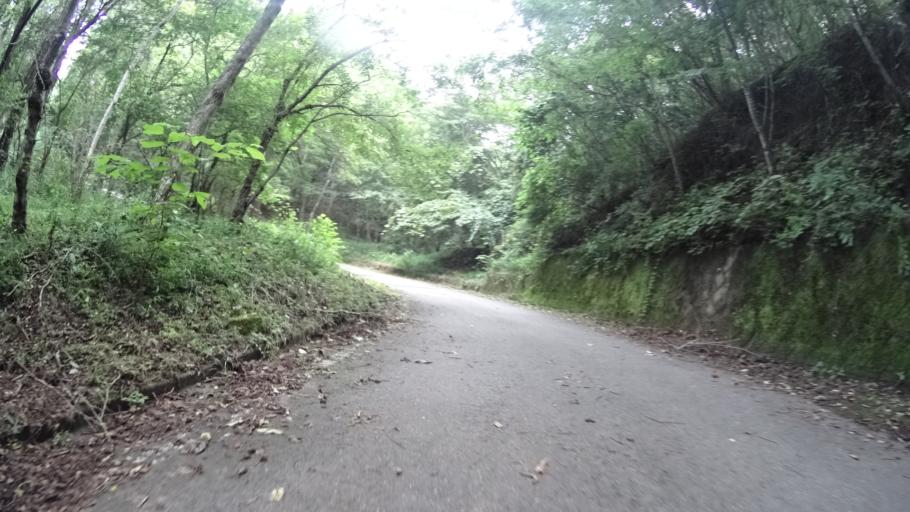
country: JP
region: Yamanashi
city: Nirasaki
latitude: 35.8806
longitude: 138.4847
